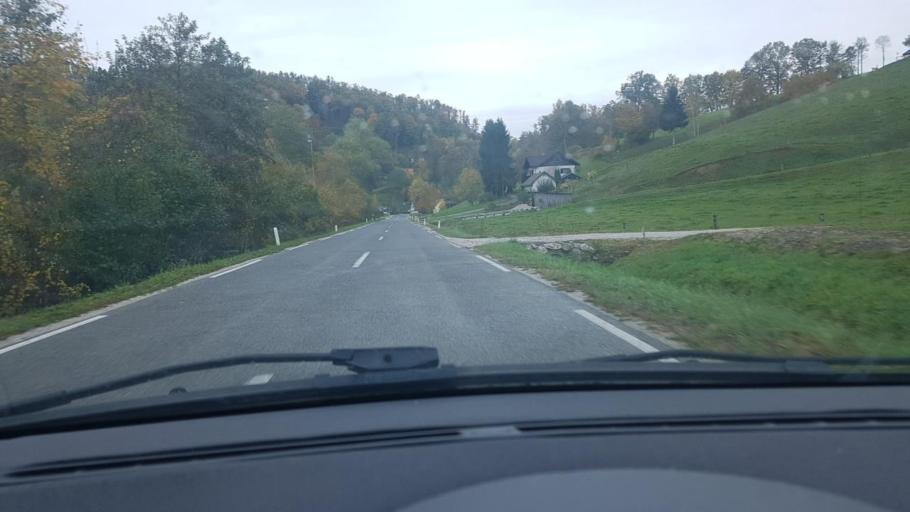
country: SI
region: Rogatec
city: Rogatec
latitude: 46.2374
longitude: 15.7025
